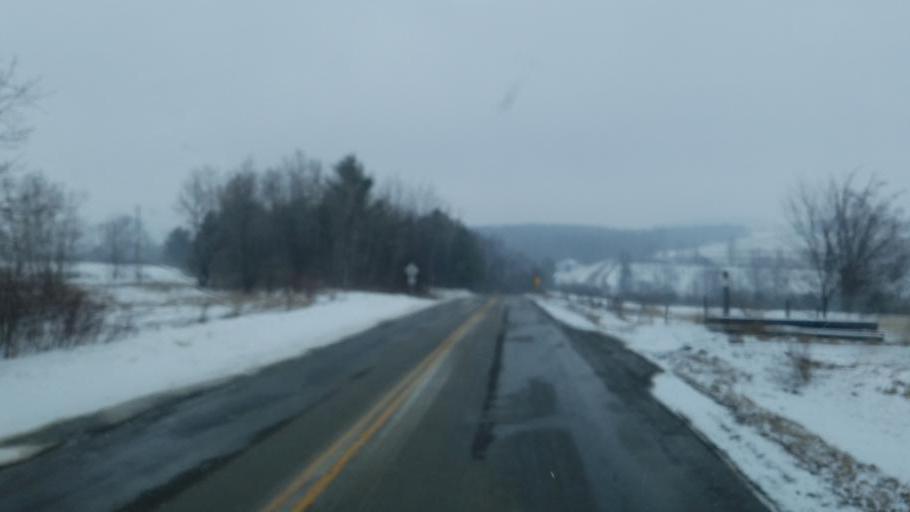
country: US
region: New York
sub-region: Steuben County
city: Canisteo
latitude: 42.1351
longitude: -77.4825
